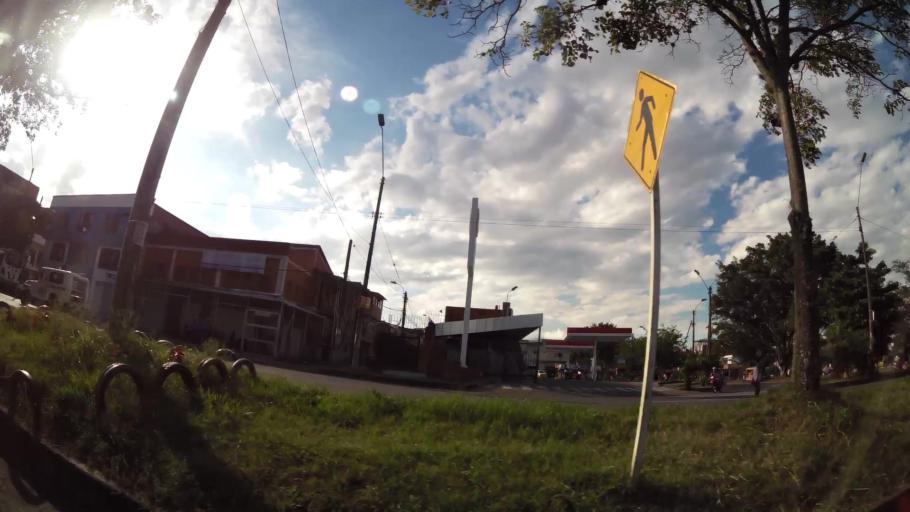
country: CO
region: Valle del Cauca
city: Cali
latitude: 3.3984
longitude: -76.5081
